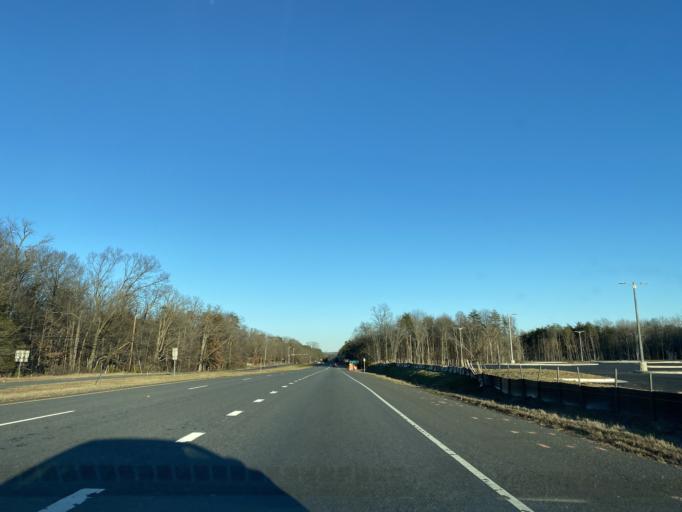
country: US
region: Virginia
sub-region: Prince William County
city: Gainesville
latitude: 38.8015
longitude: -77.5913
